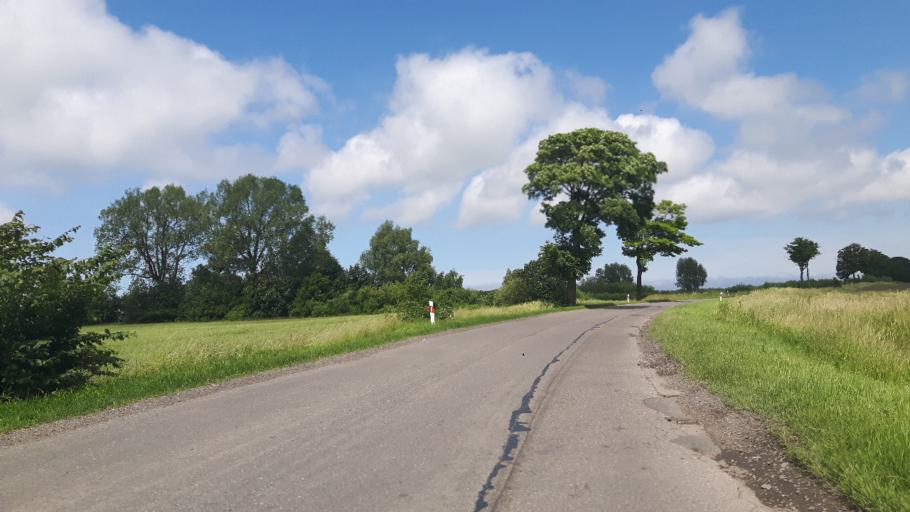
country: PL
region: Pomeranian Voivodeship
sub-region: Powiat slupski
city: Ustka
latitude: 54.5448
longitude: 16.8244
